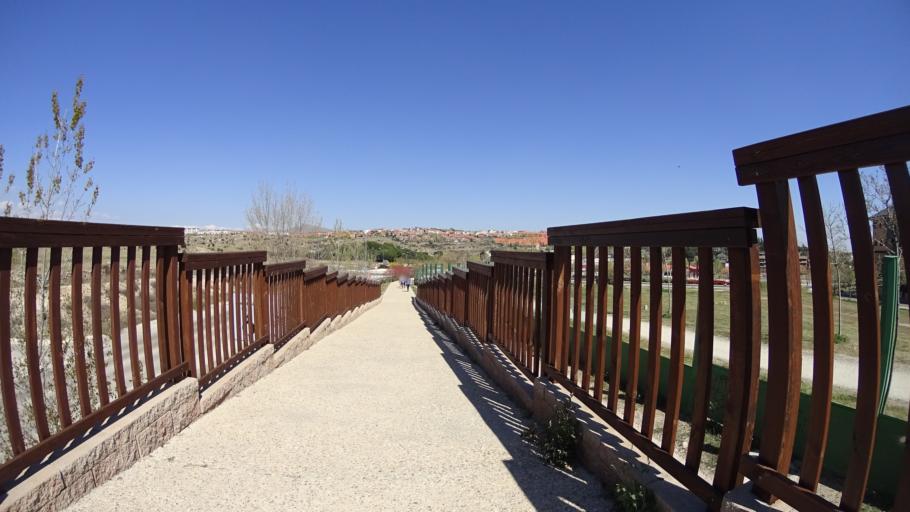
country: ES
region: Madrid
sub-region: Provincia de Madrid
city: Colmenar Viejo
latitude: 40.6526
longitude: -3.7897
